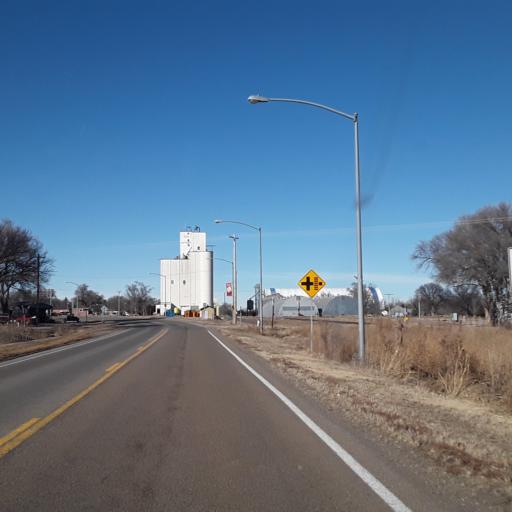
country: US
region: Nebraska
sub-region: Frontier County
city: Stockville
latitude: 40.6559
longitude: -100.6177
